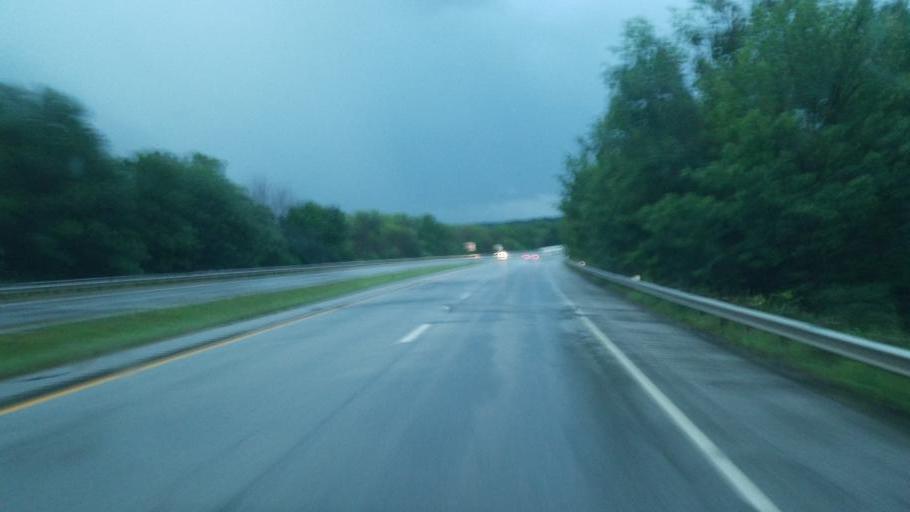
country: US
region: Ohio
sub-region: Summit County
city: Clinton
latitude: 40.9293
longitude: -81.6502
